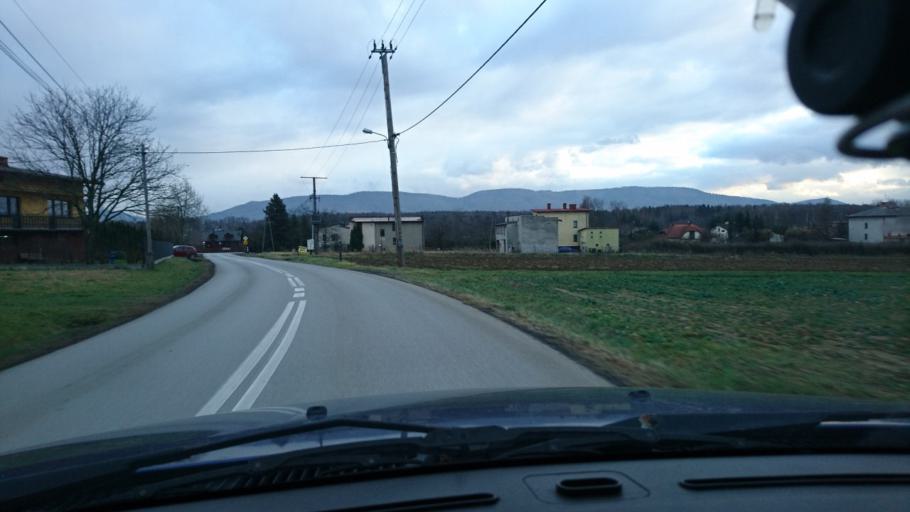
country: PL
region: Silesian Voivodeship
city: Janowice
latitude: 49.8788
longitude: 19.1023
